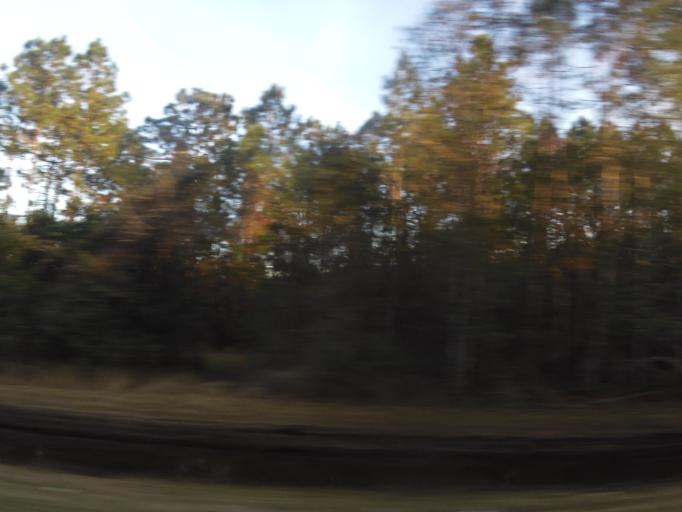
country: US
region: Florida
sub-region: Clay County
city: Green Cove Springs
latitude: 29.9461
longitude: -81.5575
